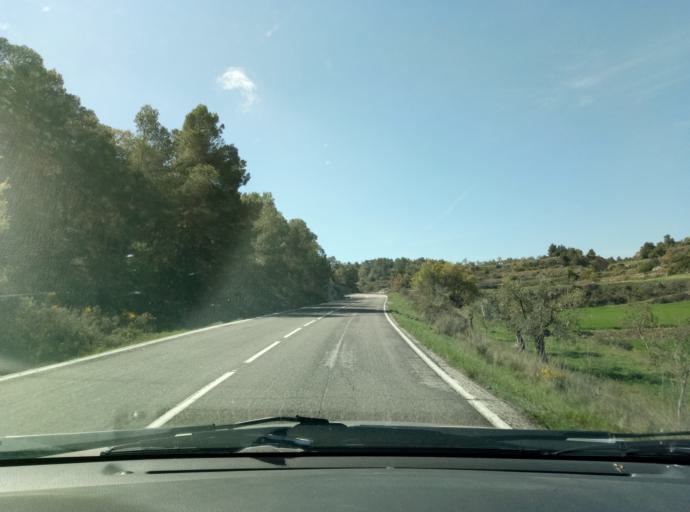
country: ES
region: Catalonia
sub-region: Provincia de Lleida
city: Fulleda
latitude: 41.5131
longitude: 1.0246
